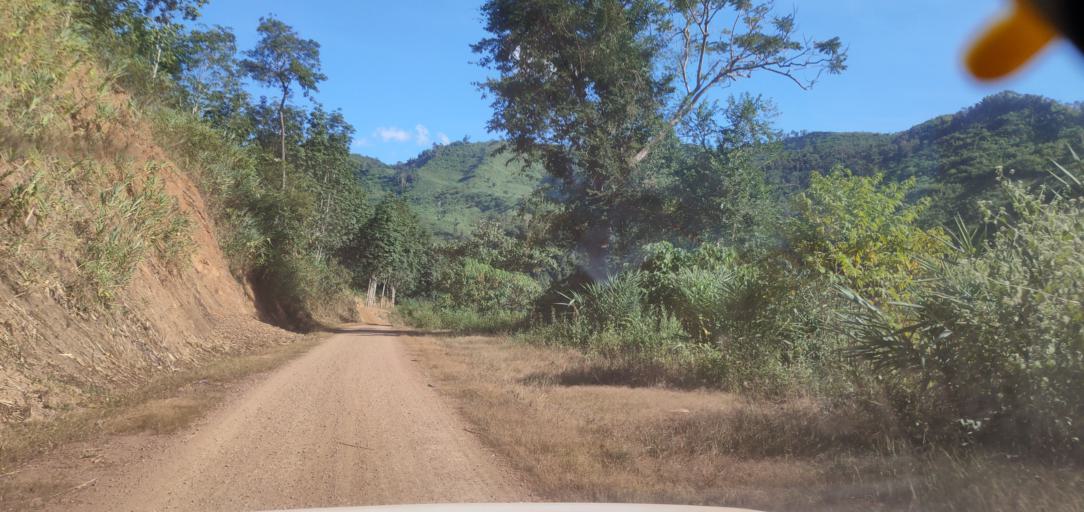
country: LA
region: Phongsali
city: Phongsali
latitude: 21.4452
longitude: 102.0538
